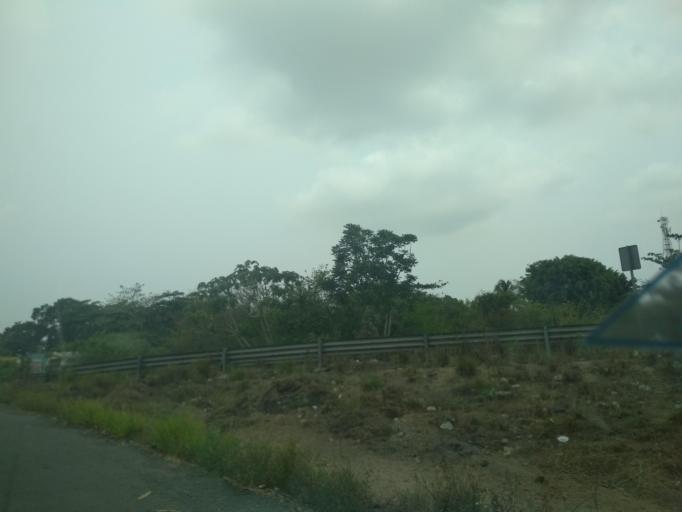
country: MX
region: Veracruz
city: Paso del Toro
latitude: 19.0252
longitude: -96.1374
